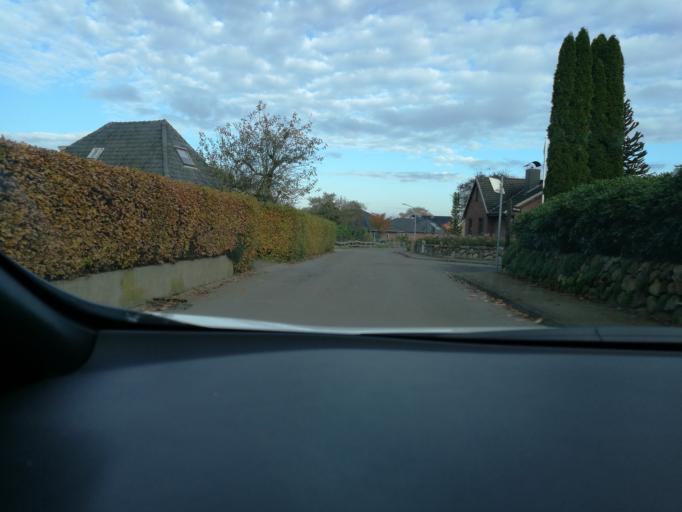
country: DE
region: Schleswig-Holstein
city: Holzbunge
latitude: 54.3822
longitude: 9.7064
